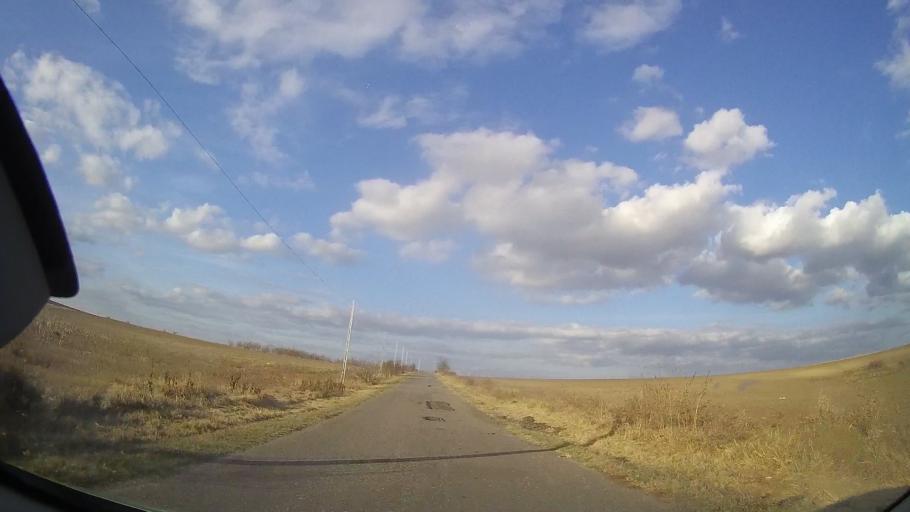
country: RO
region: Constanta
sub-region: Comuna Cerchezu
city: Cerchezu
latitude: 43.8438
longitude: 28.0985
